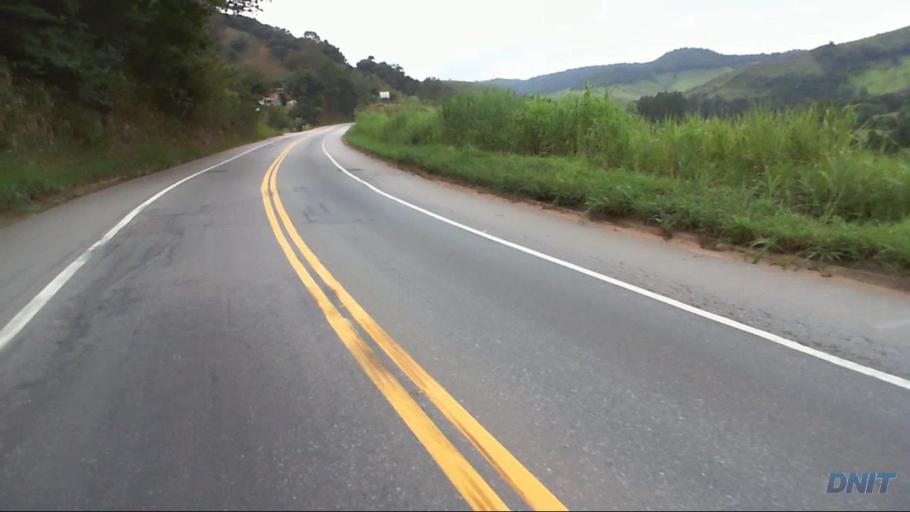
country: BR
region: Minas Gerais
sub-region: Nova Era
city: Nova Era
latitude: -19.7332
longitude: -43.0178
